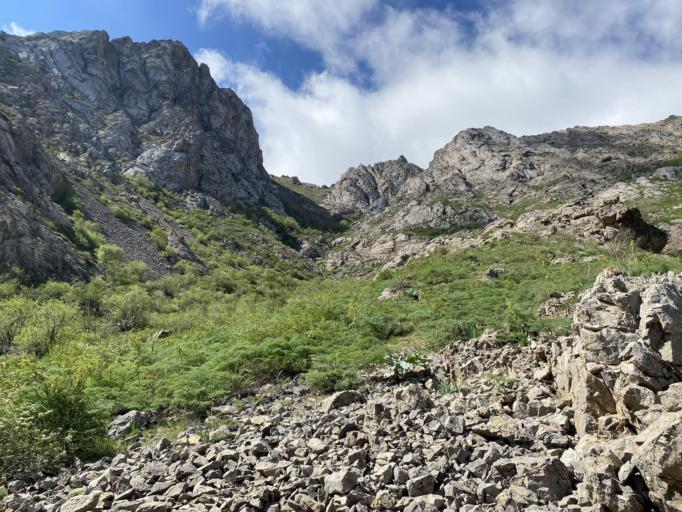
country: KZ
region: Ongtustik Qazaqstan
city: Ashchysay
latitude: 43.6452
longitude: 68.9311
